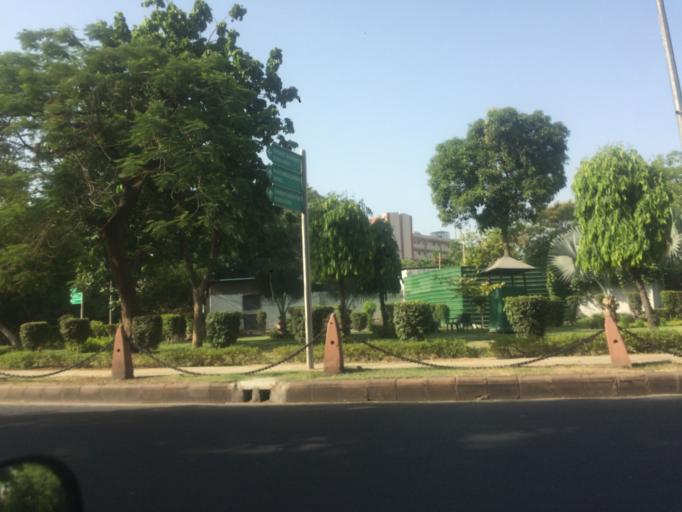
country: IN
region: NCT
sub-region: New Delhi
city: New Delhi
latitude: 28.6195
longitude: 77.2271
